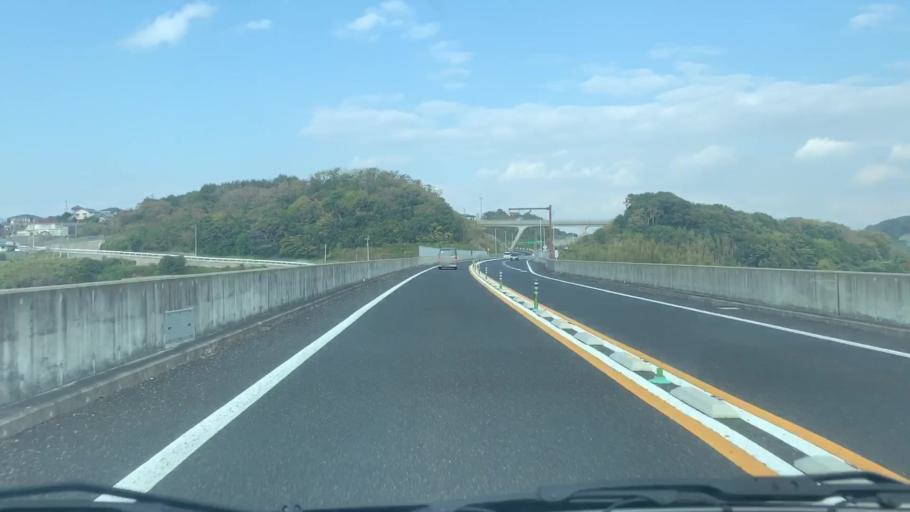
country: JP
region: Nagasaki
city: Sasebo
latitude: 33.0403
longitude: 129.7457
